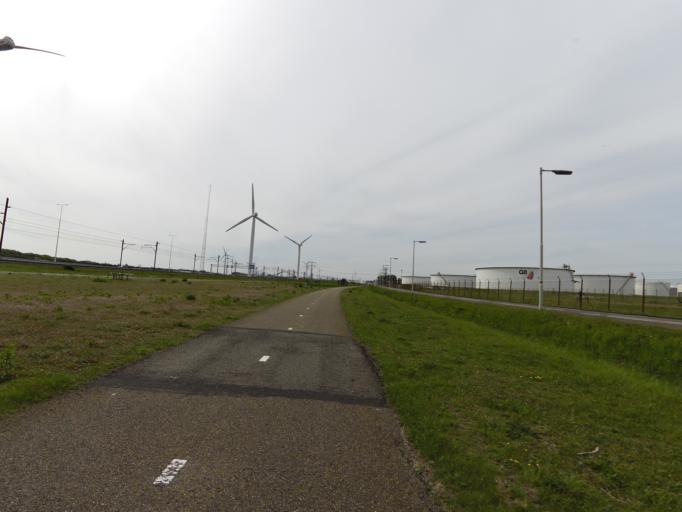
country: NL
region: South Holland
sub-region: Gemeente Brielle
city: Brielle
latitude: 51.9323
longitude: 4.1626
